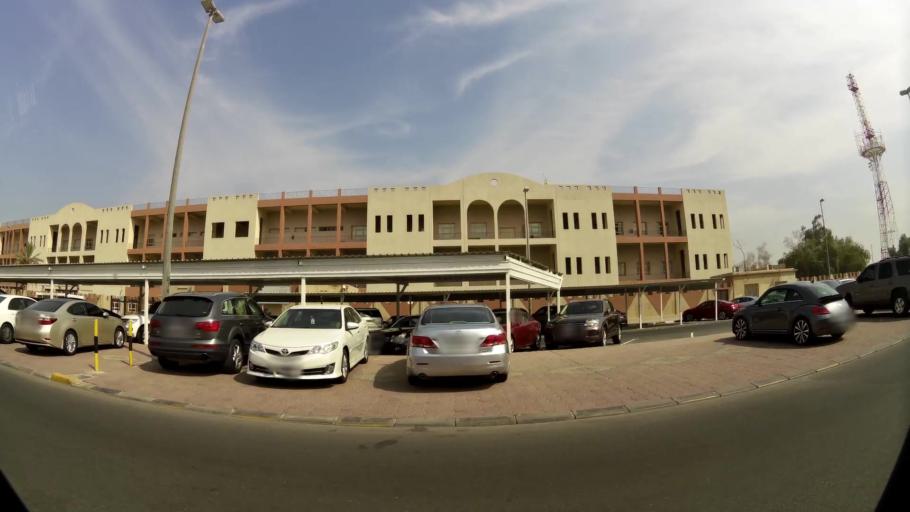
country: KW
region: Al Asimah
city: Ash Shamiyah
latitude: 29.3397
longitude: 47.9783
